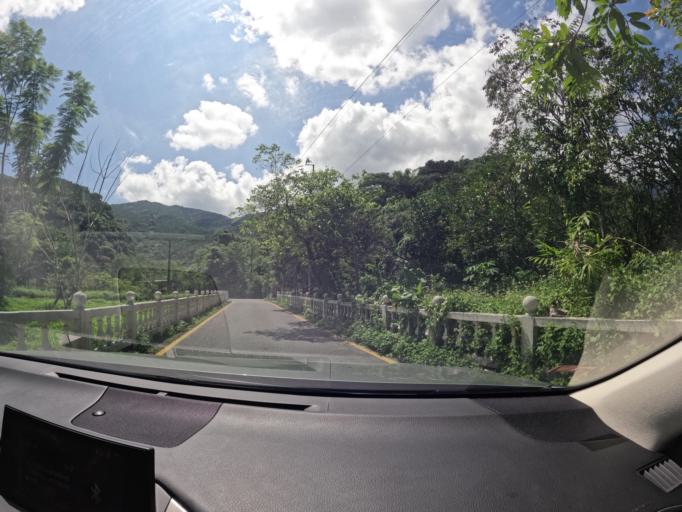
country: TW
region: Taiwan
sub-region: Hualien
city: Hualian
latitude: 23.6818
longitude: 121.3969
